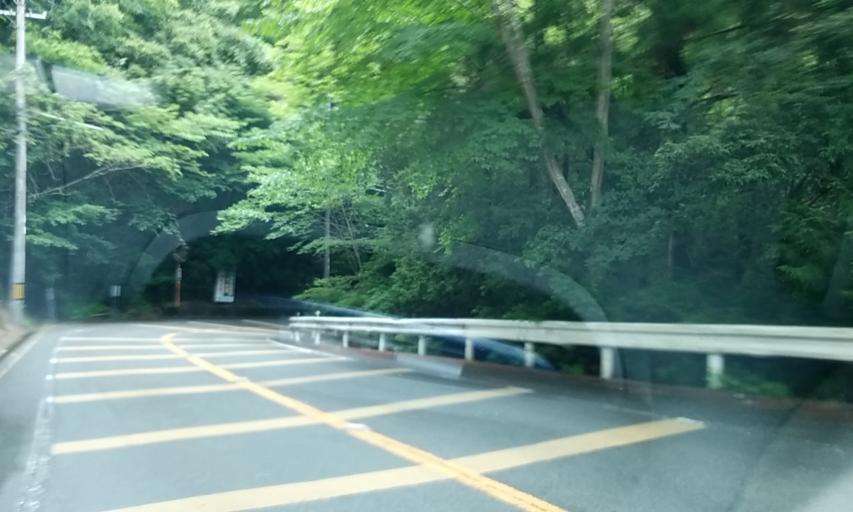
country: JP
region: Kyoto
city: Kameoka
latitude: 35.0390
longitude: 135.4089
